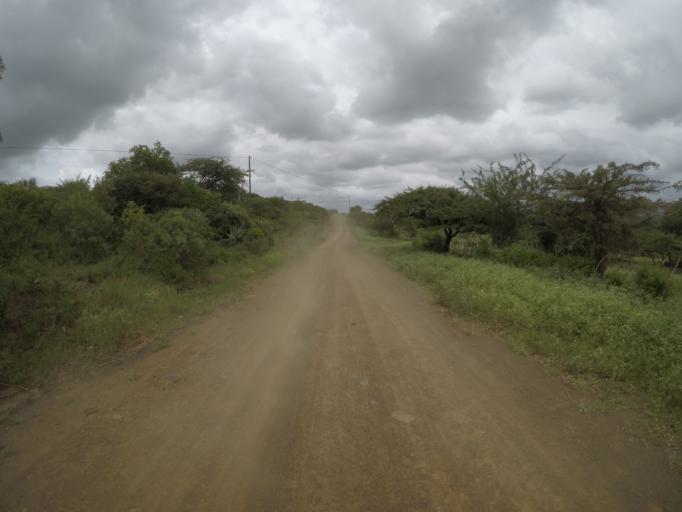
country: ZA
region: KwaZulu-Natal
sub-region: uThungulu District Municipality
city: Empangeni
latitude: -28.5776
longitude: 31.8699
